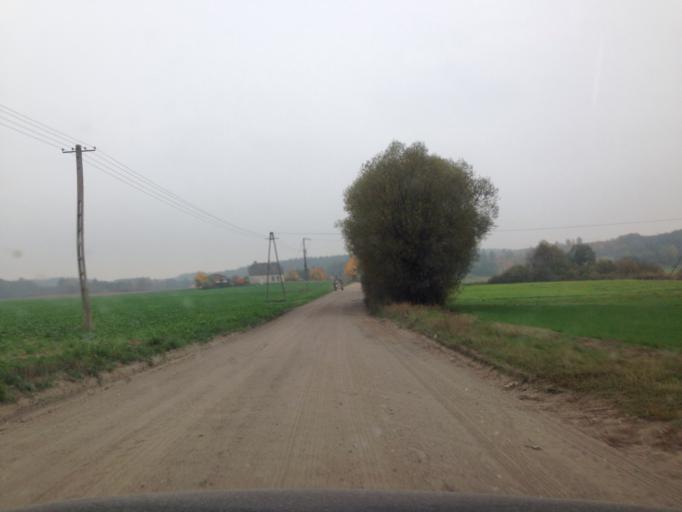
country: PL
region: Kujawsko-Pomorskie
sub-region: Powiat brodnicki
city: Bartniczka
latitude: 53.2580
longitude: 19.5893
